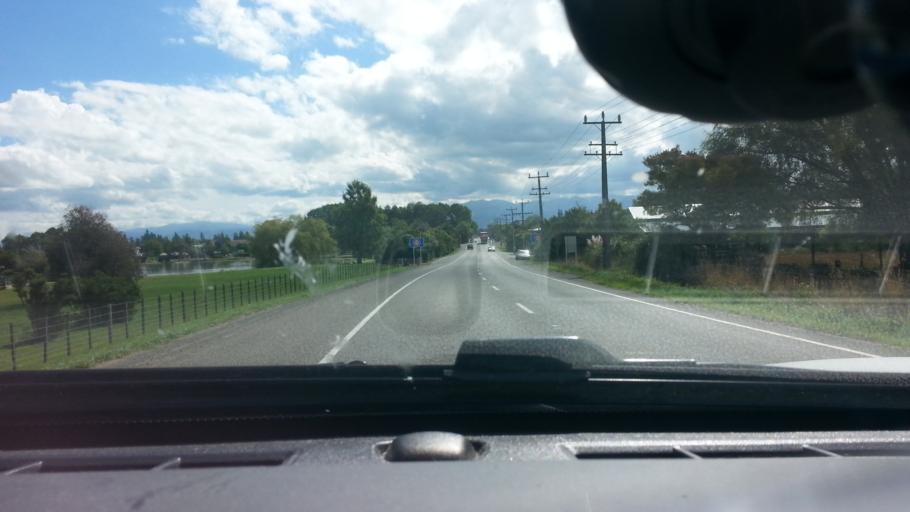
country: NZ
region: Wellington
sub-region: Masterton District
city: Masterton
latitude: -40.9495
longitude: 175.6858
